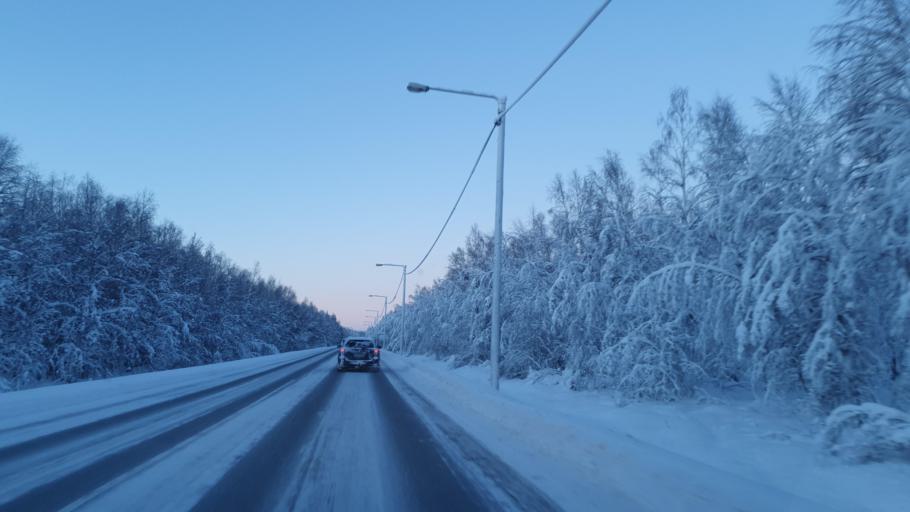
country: FI
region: Lapland
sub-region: Kemi-Tornio
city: Tornio
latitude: 66.0147
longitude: 24.0649
